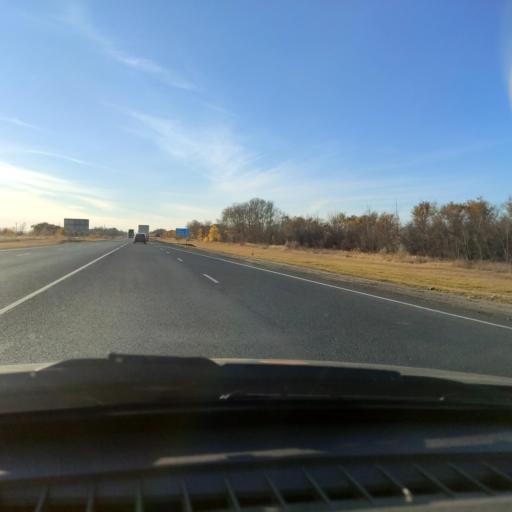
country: RU
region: Samara
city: Varlamovo
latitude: 53.1956
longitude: 48.2815
